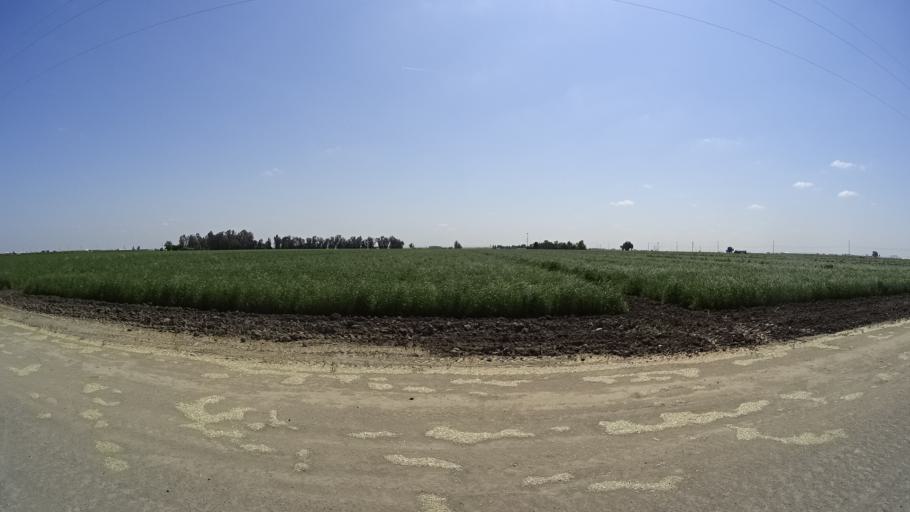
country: US
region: California
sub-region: Kings County
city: Home Garden
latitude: 36.2132
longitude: -119.6279
